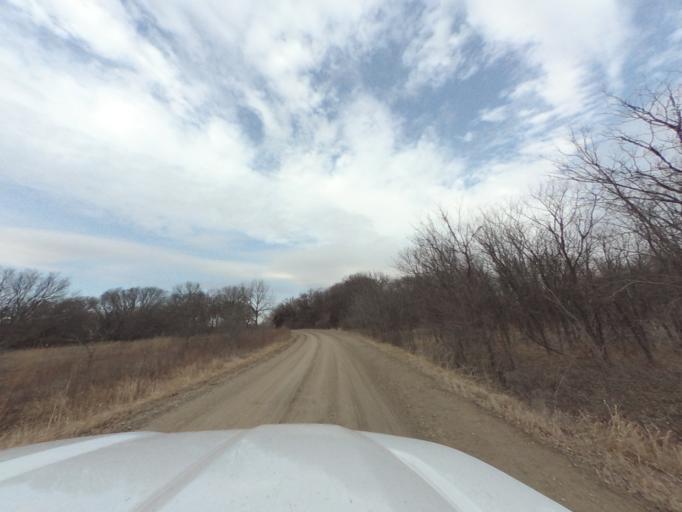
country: US
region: Kansas
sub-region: Chase County
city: Cottonwood Falls
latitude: 38.2744
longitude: -96.7322
